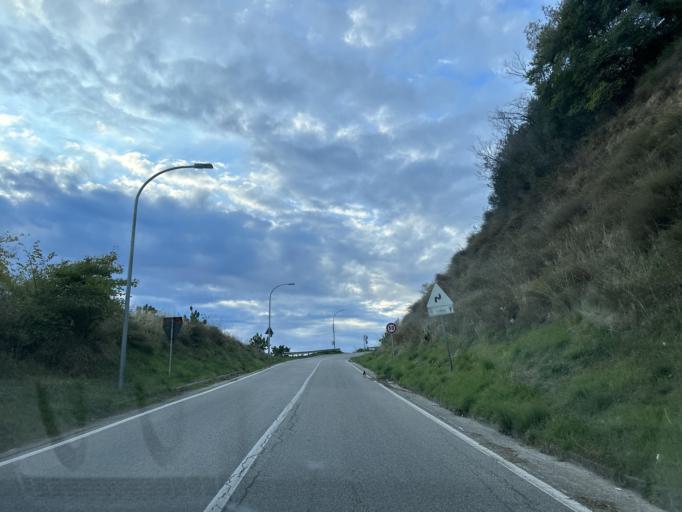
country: IT
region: Calabria
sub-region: Provincia di Catanzaro
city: Montauro
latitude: 38.7493
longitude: 16.5098
